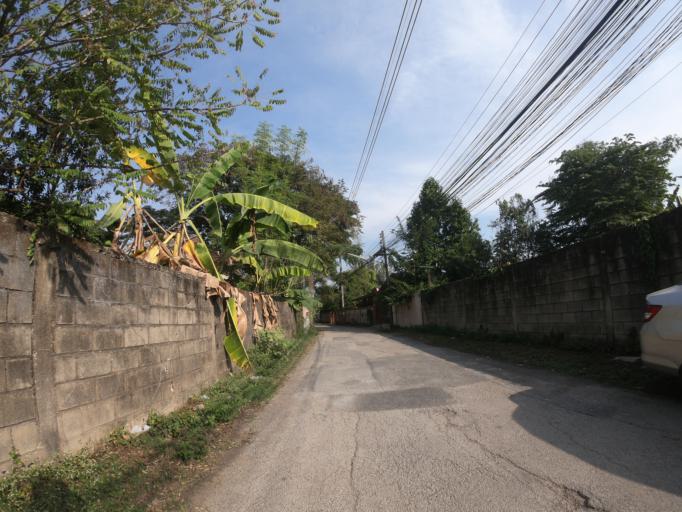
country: TH
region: Chiang Mai
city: Chiang Mai
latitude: 18.7707
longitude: 99.0209
